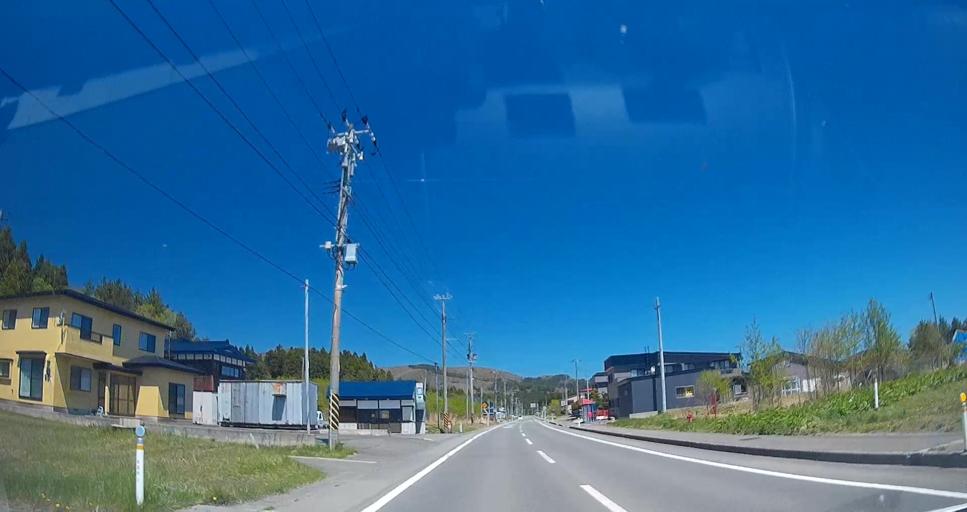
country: JP
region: Aomori
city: Mutsu
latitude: 41.0810
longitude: 141.3857
